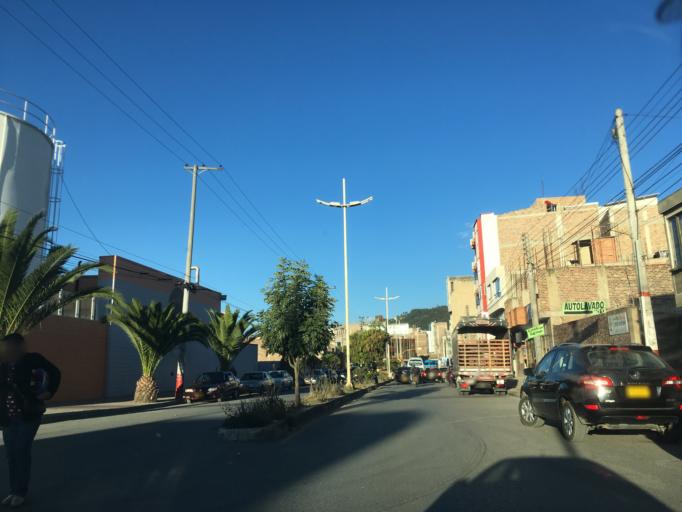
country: CO
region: Boyaca
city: Sogamoso
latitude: 5.7121
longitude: -72.9308
